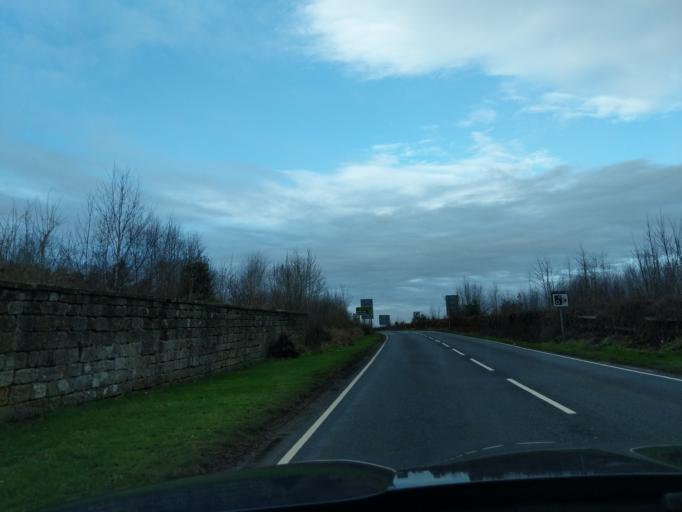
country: GB
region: England
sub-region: Northumberland
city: Meldon
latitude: 55.1058
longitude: -1.8444
